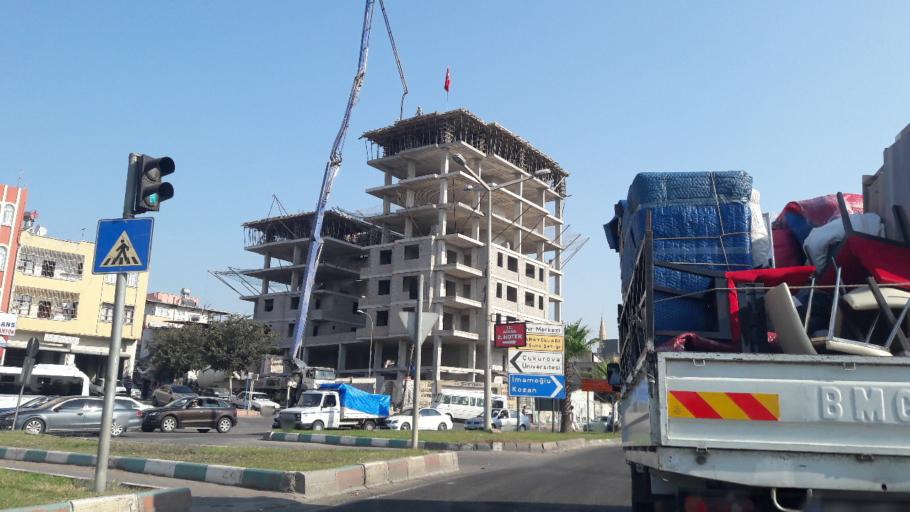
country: TR
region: Adana
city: Yuregir
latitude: 37.0252
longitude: 35.3996
